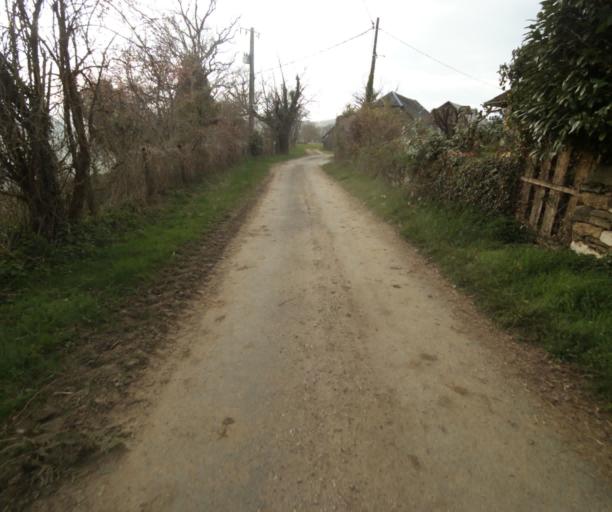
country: FR
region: Limousin
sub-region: Departement de la Correze
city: Saint-Clement
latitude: 45.3654
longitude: 1.6309
